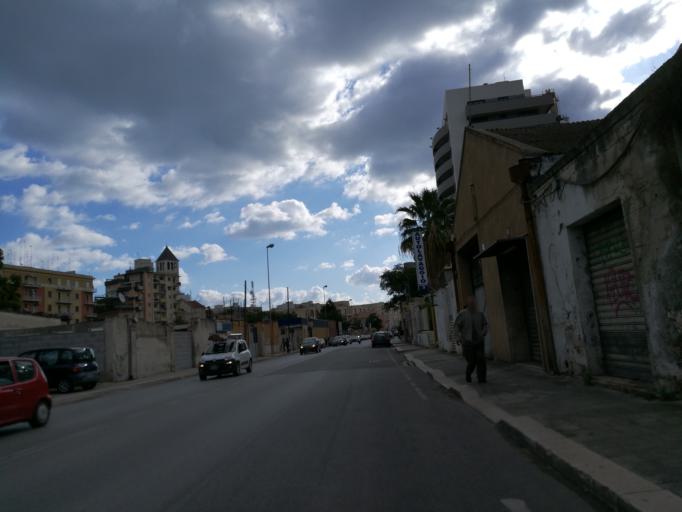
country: IT
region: Apulia
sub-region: Provincia di Bari
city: Bari
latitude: 41.1176
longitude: 16.8802
